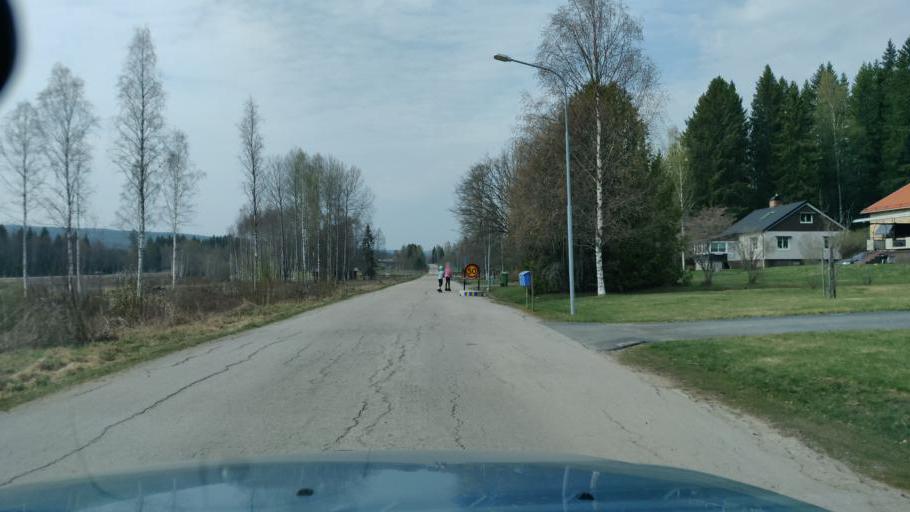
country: SE
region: Vaermland
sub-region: Munkfors Kommun
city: Munkfors
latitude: 59.8365
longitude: 13.5084
